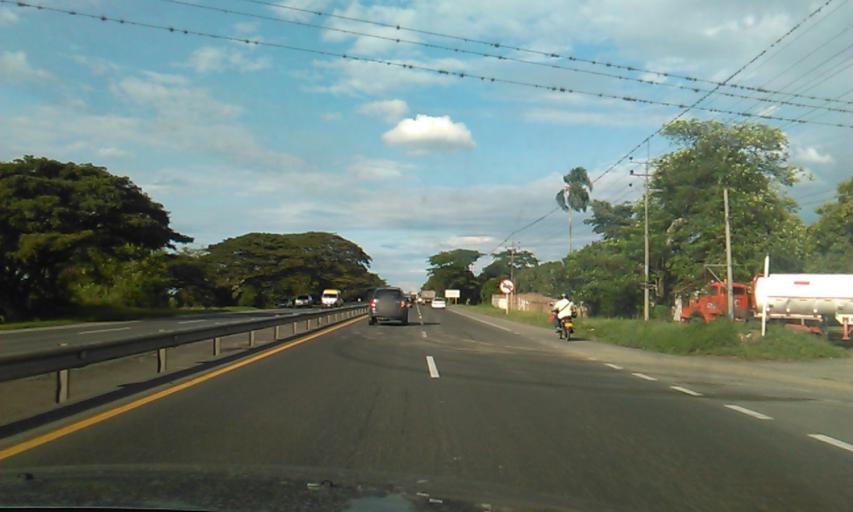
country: CO
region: Valle del Cauca
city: Buga
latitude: 3.9037
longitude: -76.3108
